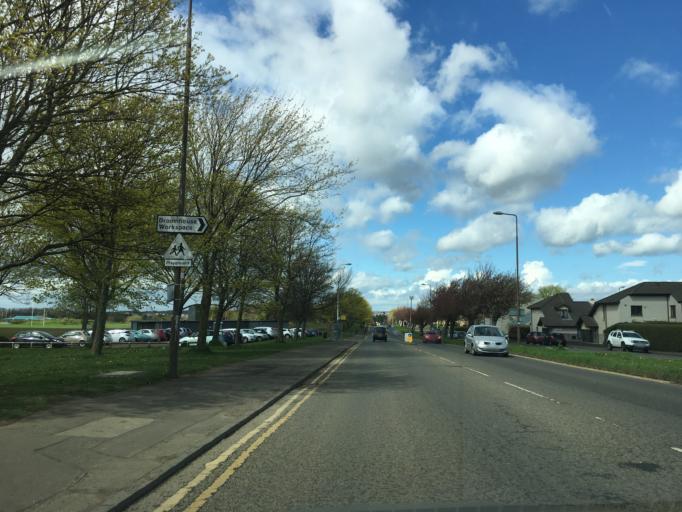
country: GB
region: Scotland
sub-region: Edinburgh
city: Colinton
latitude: 55.9253
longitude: -3.2824
